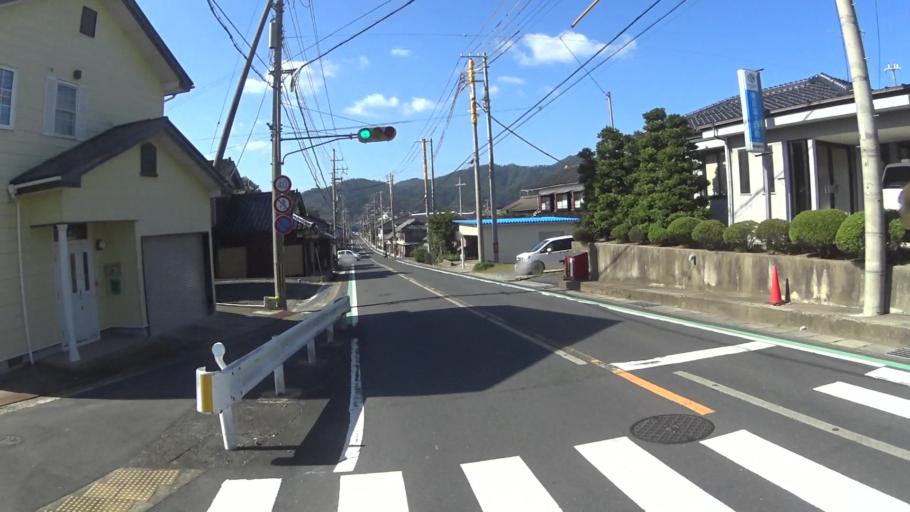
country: JP
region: Kyoto
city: Miyazu
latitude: 35.6823
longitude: 135.0339
